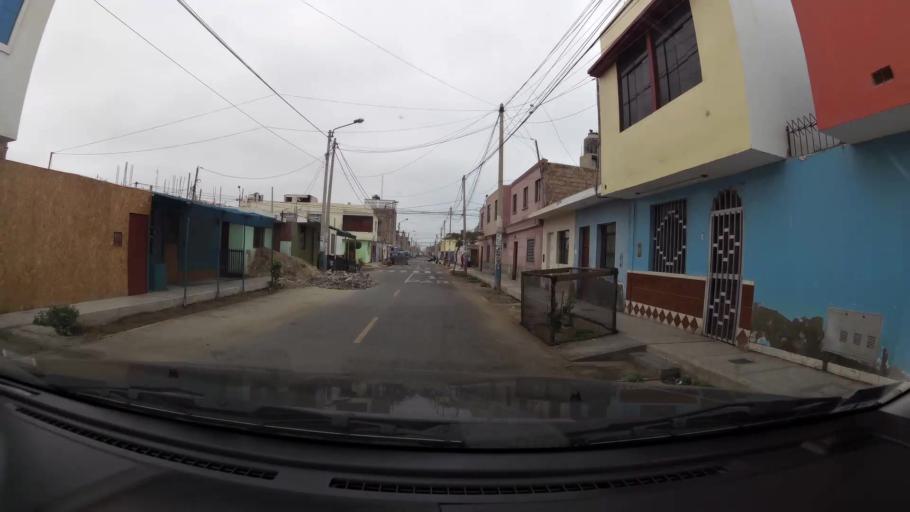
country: PE
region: Ica
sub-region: Provincia de Pisco
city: Pisco
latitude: -13.7330
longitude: -76.2224
